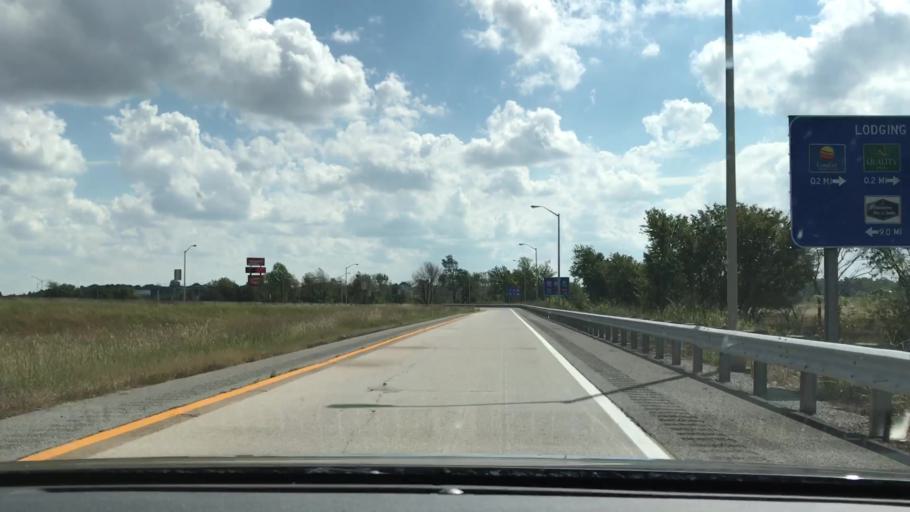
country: US
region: Kentucky
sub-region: Christian County
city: Oak Grove
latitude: 36.7029
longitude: -87.4583
